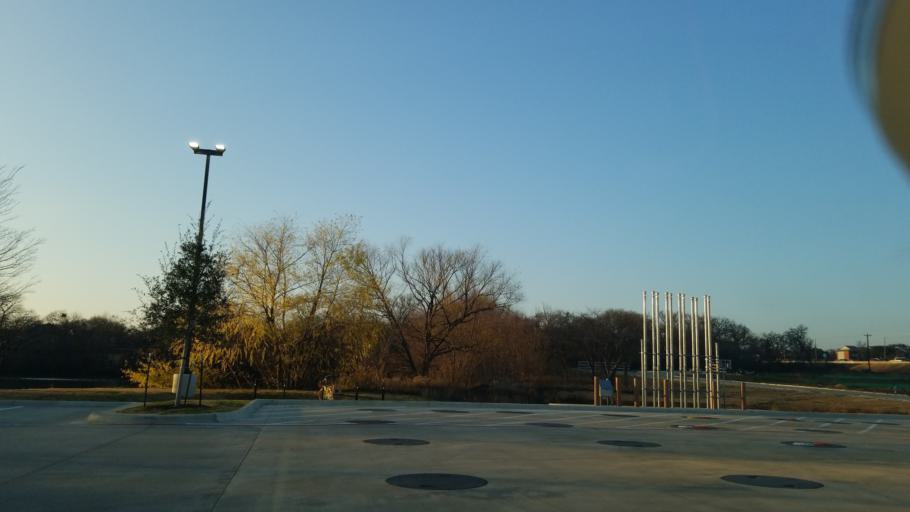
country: US
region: Texas
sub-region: Denton County
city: Denton
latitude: 33.1802
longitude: -97.1032
